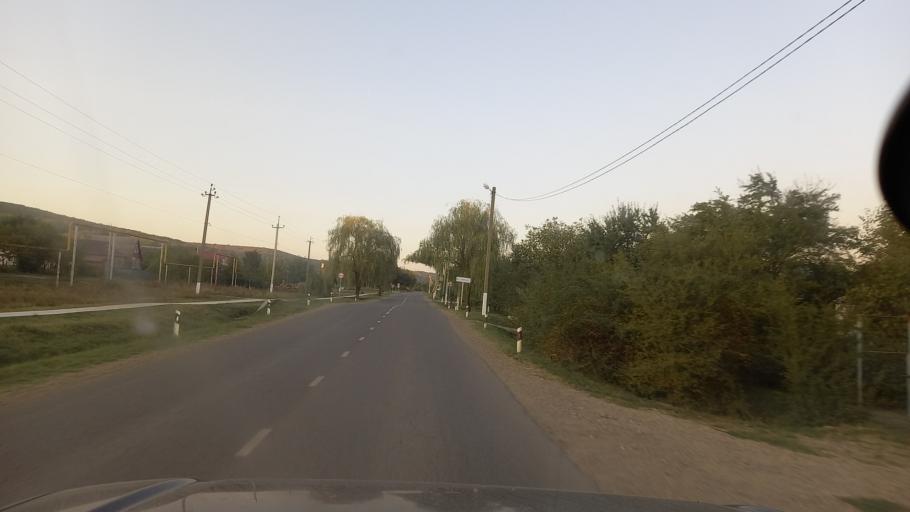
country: RU
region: Krasnodarskiy
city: Smolenskaya
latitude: 44.7737
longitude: 38.7856
